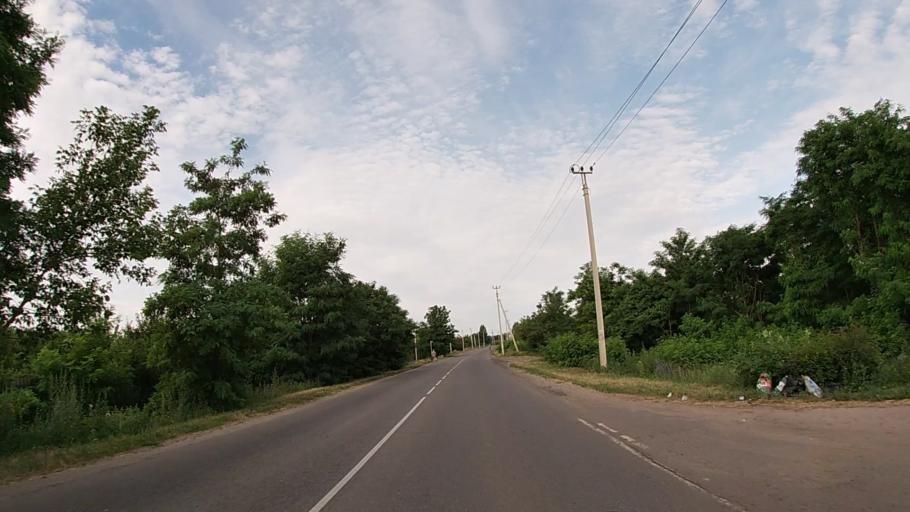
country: RU
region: Belgorod
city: Severnyy
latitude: 50.6950
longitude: 36.5713
